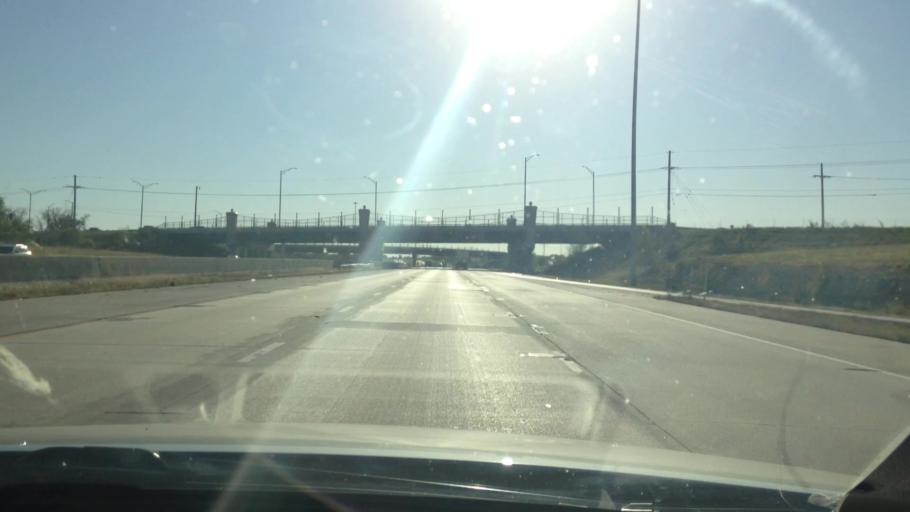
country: US
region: Kansas
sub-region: Johnson County
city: Olathe
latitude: 38.8425
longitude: -94.8325
